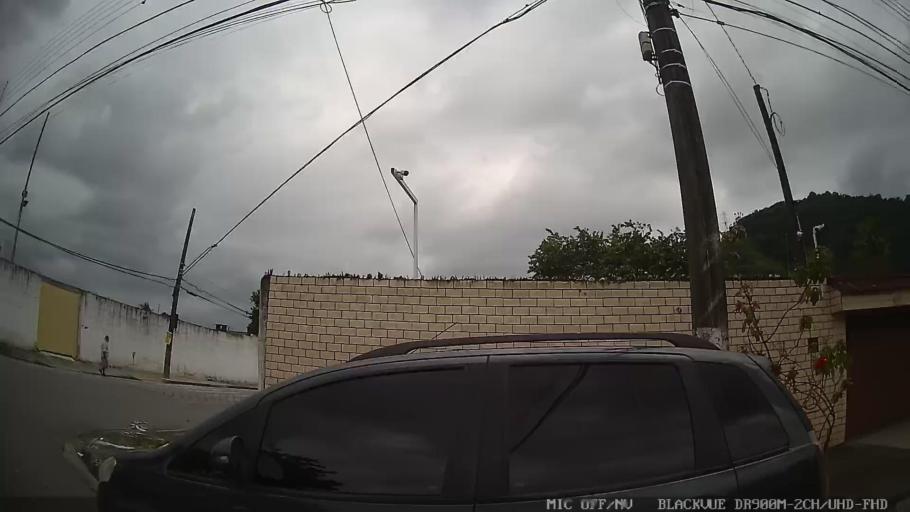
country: BR
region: Sao Paulo
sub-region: Guaruja
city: Guaruja
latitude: -23.9936
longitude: -46.2721
